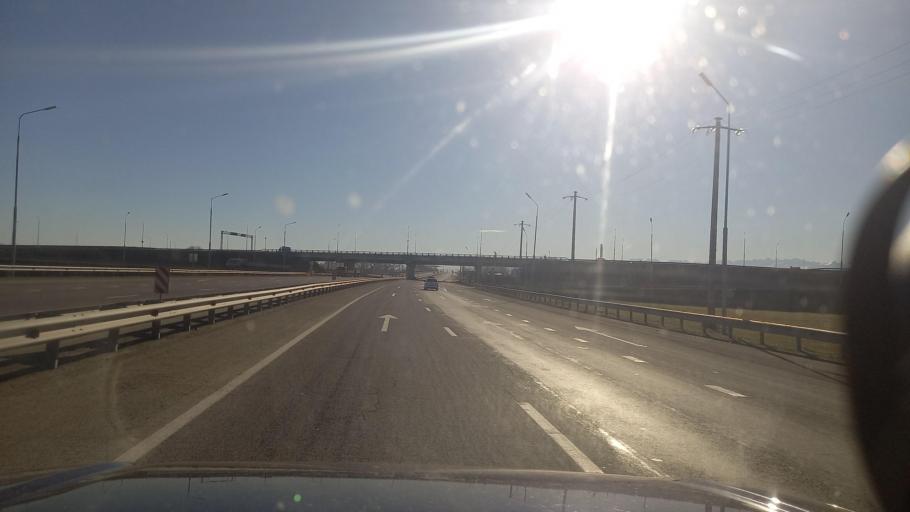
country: RU
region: Kabardino-Balkariya
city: Germenchik
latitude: 43.5686
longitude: 43.7173
